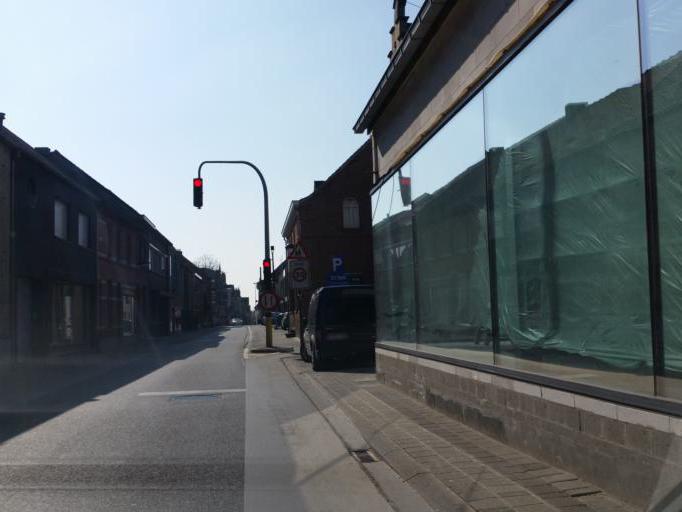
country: BE
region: Flanders
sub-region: Provincie Oost-Vlaanderen
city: Kruibeke
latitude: 51.1731
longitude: 4.3141
